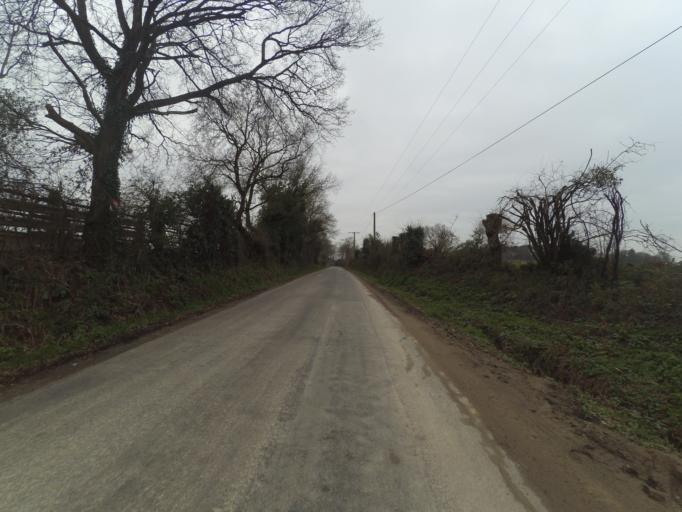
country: FR
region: Pays de la Loire
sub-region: Departement de la Loire-Atlantique
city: Sautron
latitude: 47.2590
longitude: -1.7065
